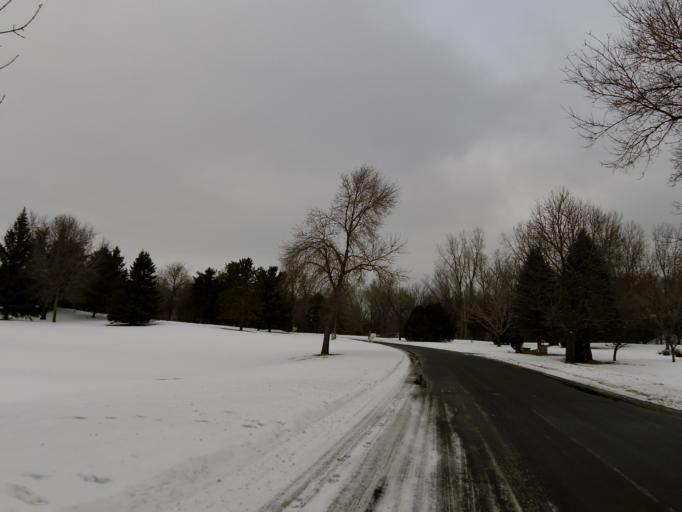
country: US
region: Minnesota
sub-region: Washington County
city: Lake Elmo
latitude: 44.9604
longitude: -92.8475
